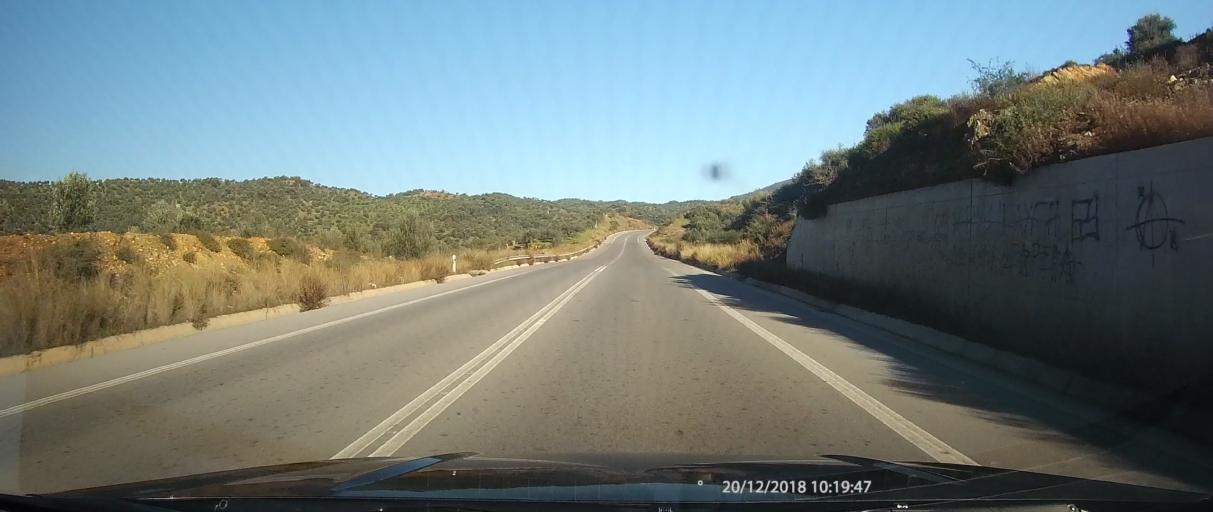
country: GR
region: Peloponnese
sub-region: Nomos Lakonias
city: Magoula
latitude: 37.1395
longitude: 22.4248
